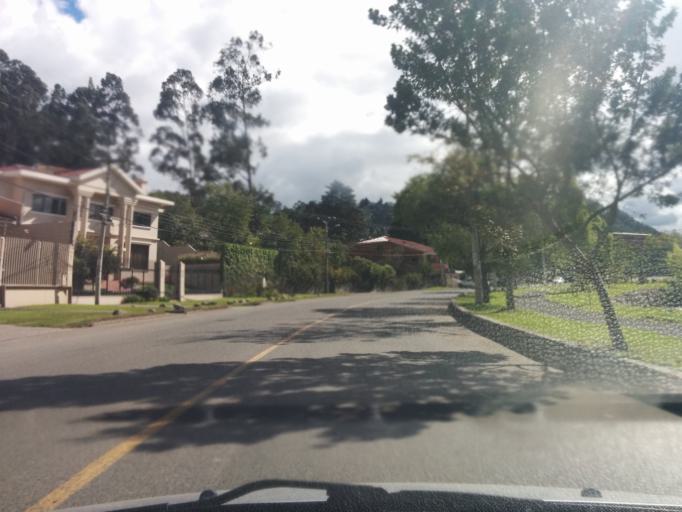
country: EC
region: Azuay
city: Cuenca
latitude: -2.9173
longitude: -78.9983
